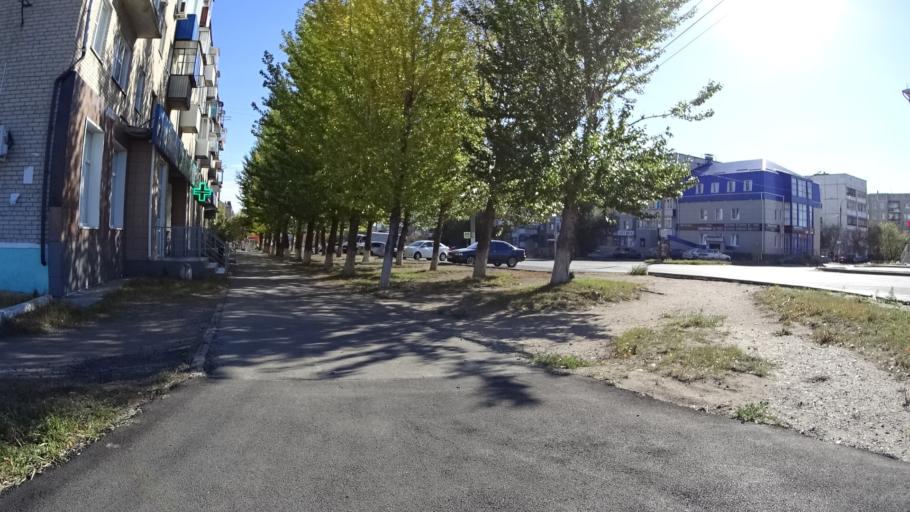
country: RU
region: Chelyabinsk
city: Troitsk
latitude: 54.0801
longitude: 61.5290
